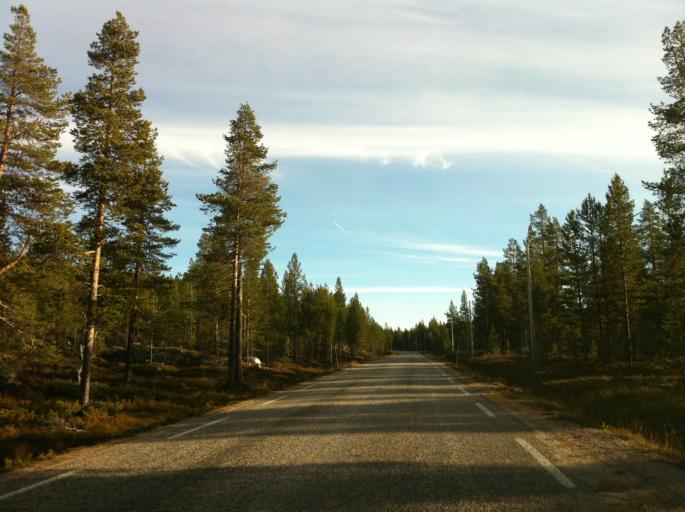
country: NO
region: Hedmark
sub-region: Engerdal
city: Engerdal
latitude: 62.1464
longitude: 11.9590
